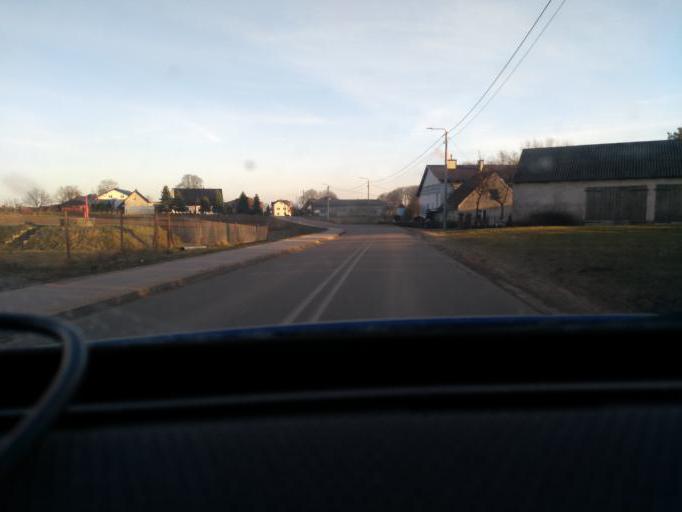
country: PL
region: Pomeranian Voivodeship
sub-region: Powiat kartuski
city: Przodkowo
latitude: 54.4130
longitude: 18.3206
